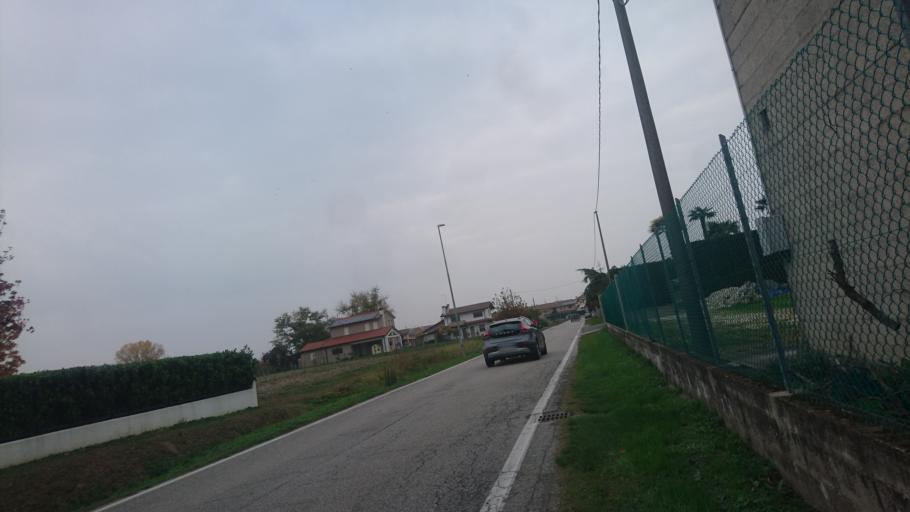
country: IT
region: Veneto
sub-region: Provincia di Venezia
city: Tombelle
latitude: 45.3918
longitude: 11.9794
